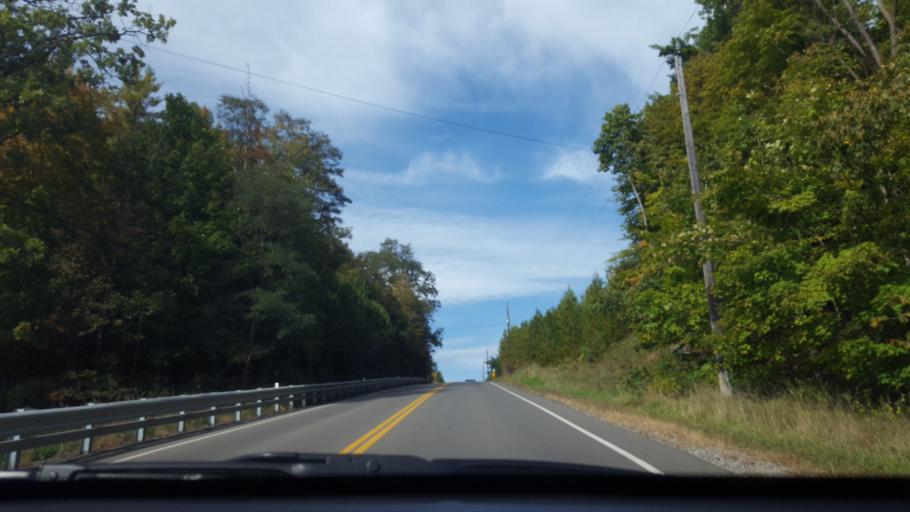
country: CA
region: Ontario
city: Vaughan
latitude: 43.8465
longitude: -79.5879
